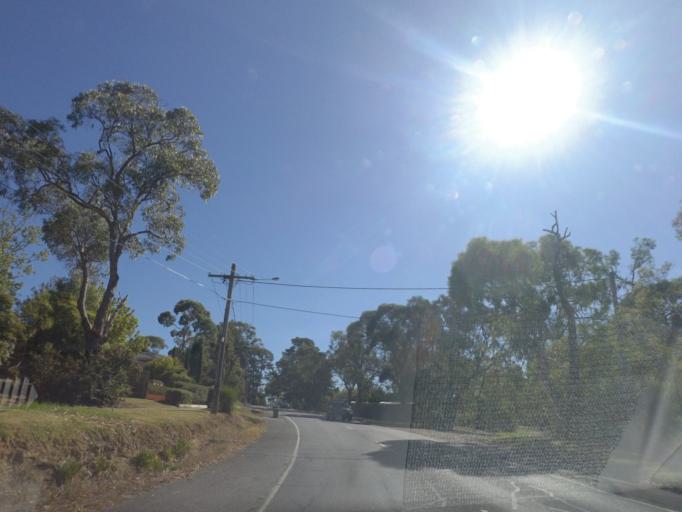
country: AU
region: Victoria
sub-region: Maroondah
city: Croydon North
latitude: -37.7874
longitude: 145.2943
